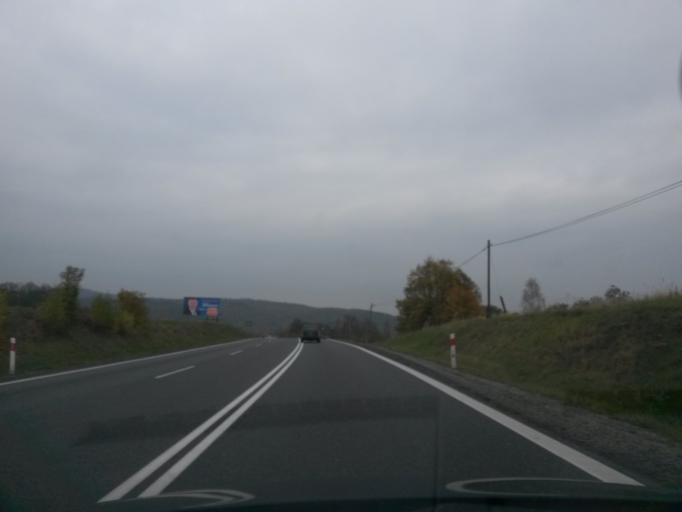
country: PL
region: Lower Silesian Voivodeship
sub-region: Powiat zabkowicki
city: Bardo
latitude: 50.4962
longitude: 16.7245
